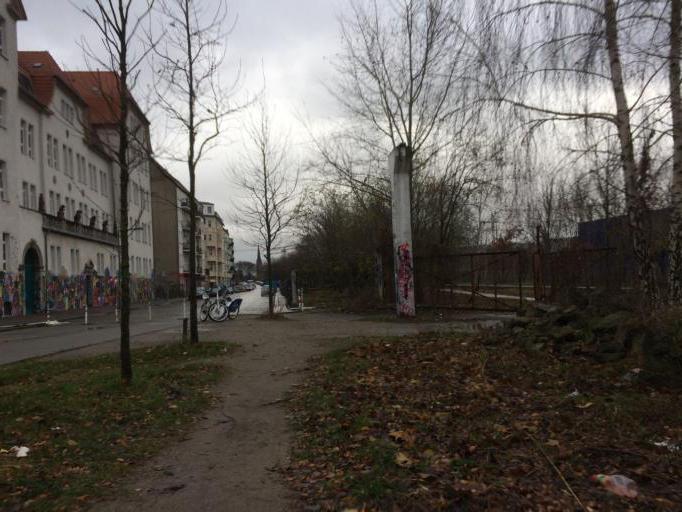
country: DE
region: Berlin
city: Friedrichshain Bezirk
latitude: 52.5104
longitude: 13.4448
